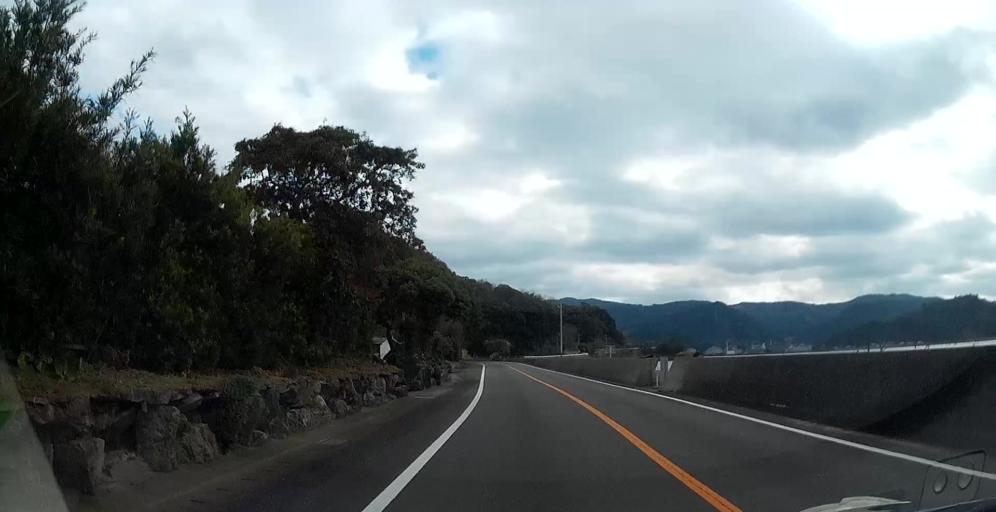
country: JP
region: Kumamoto
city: Minamata
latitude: 32.3623
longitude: 130.4960
